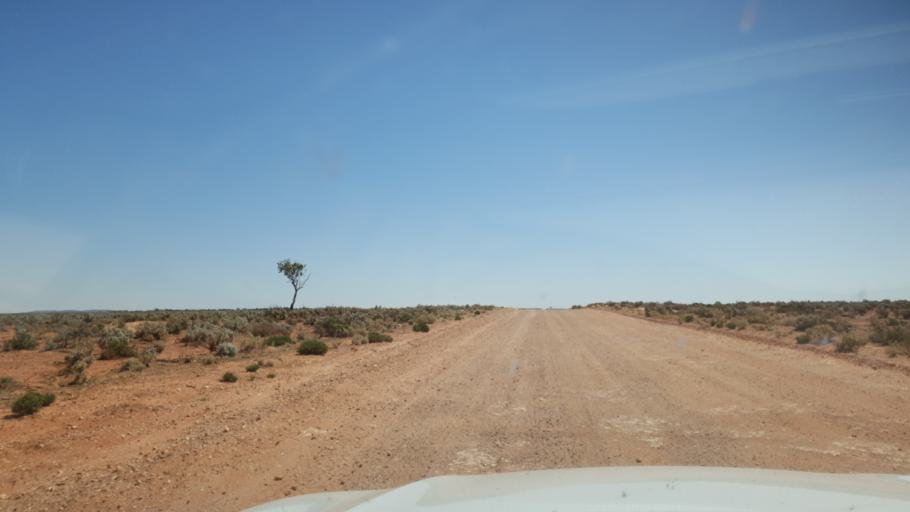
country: AU
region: South Australia
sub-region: Whyalla
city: Whyalla
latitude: -32.6464
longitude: 136.9558
